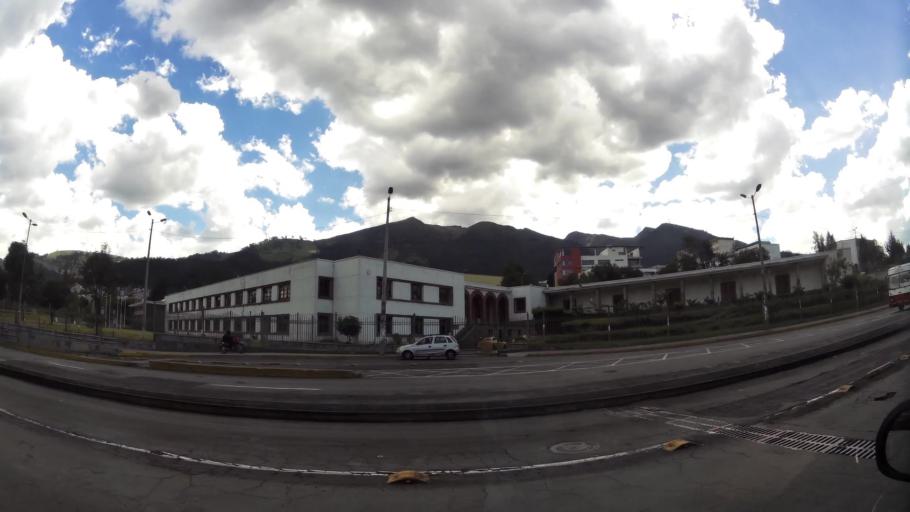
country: EC
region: Pichincha
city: Quito
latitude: -0.2006
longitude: -78.5010
